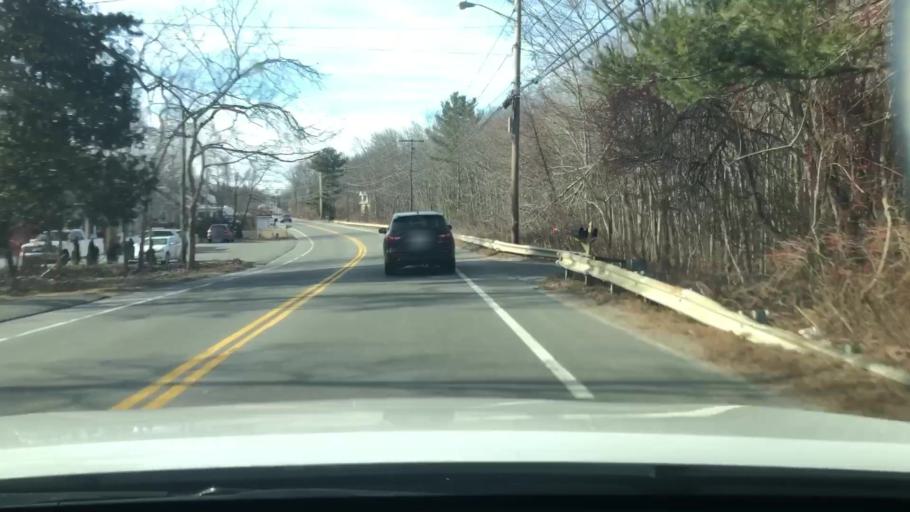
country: US
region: Massachusetts
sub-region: Worcester County
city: Grafton
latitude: 42.2062
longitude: -71.6763
